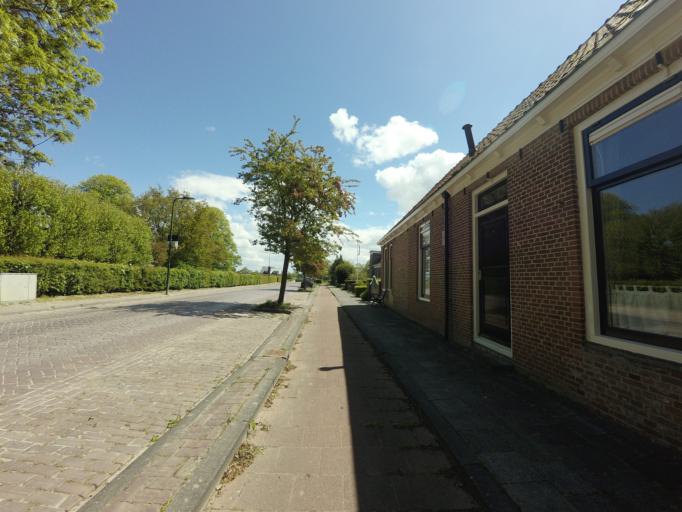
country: NL
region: Friesland
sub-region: Gemeente Harlingen
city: Harlingen
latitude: 53.1411
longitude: 5.4392
